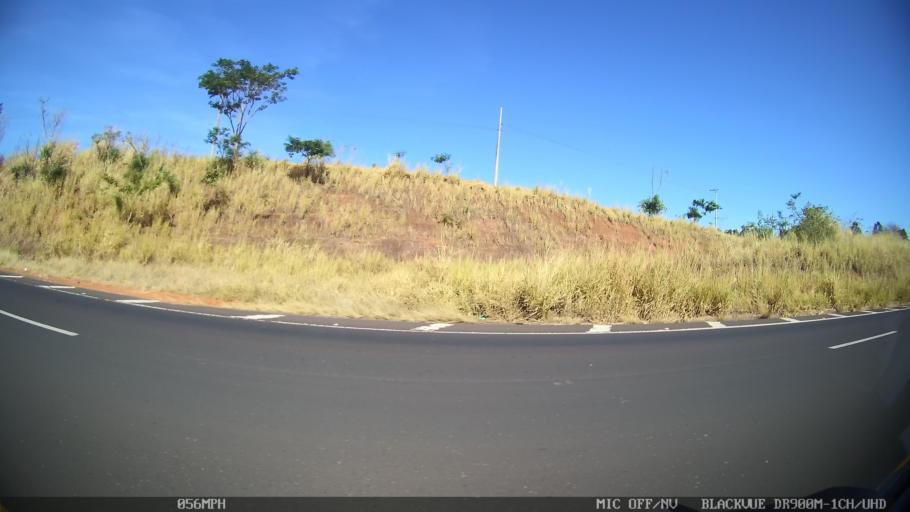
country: BR
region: Sao Paulo
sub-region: Barretos
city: Barretos
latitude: -20.6097
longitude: -48.7499
